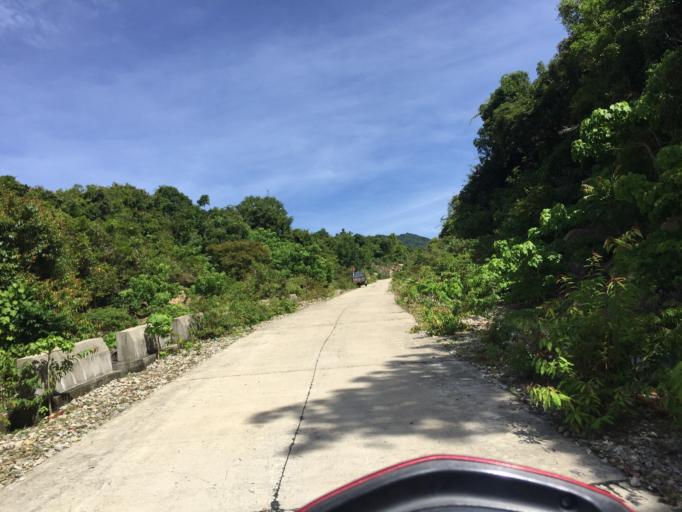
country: VN
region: Quang Nam
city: Hoi An
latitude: 15.9350
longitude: 108.5310
